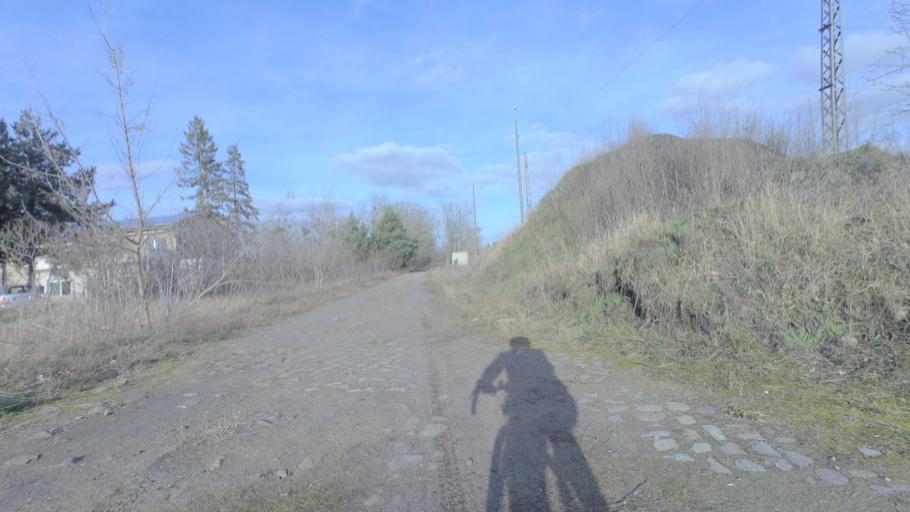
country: DE
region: Brandenburg
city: Trebbin
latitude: 52.2193
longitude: 13.2310
